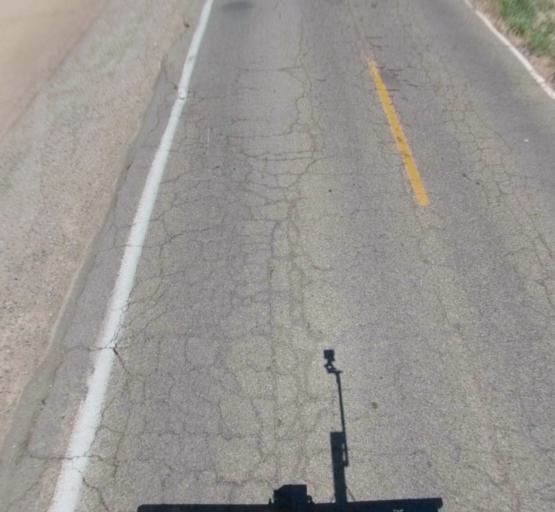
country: US
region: California
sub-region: Madera County
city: Fairmead
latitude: 37.0183
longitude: -120.2003
